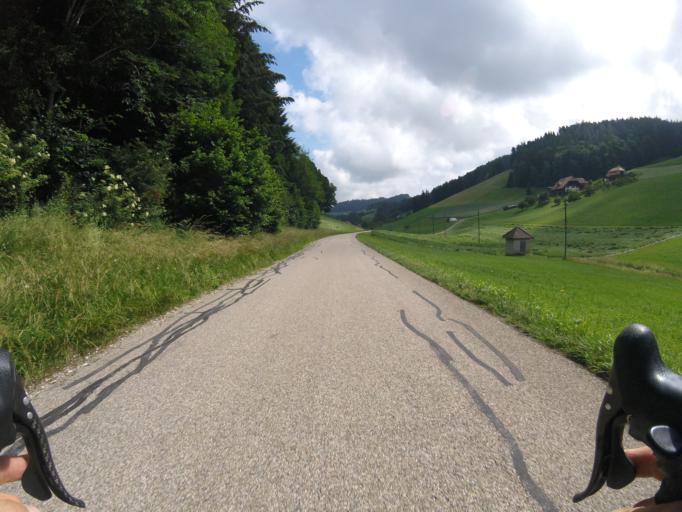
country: CH
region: Bern
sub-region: Emmental District
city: Krauchthal
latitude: 46.9949
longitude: 7.5865
